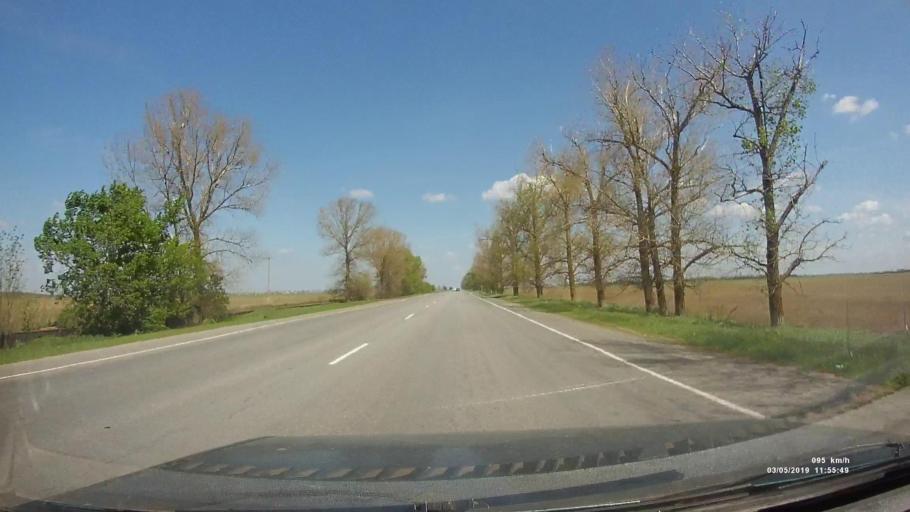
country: RU
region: Rostov
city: Bagayevskaya
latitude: 47.1860
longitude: 40.2947
